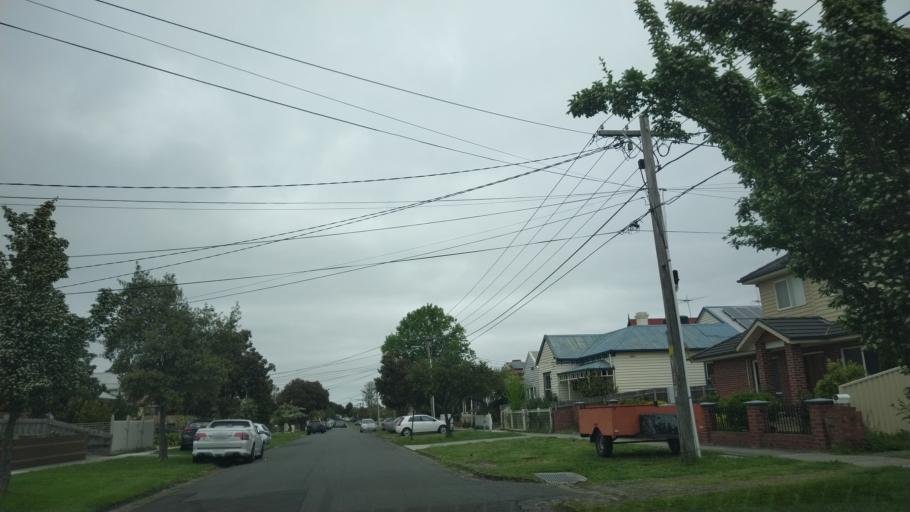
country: AU
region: Victoria
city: Hughesdale
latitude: -37.9016
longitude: 145.0840
